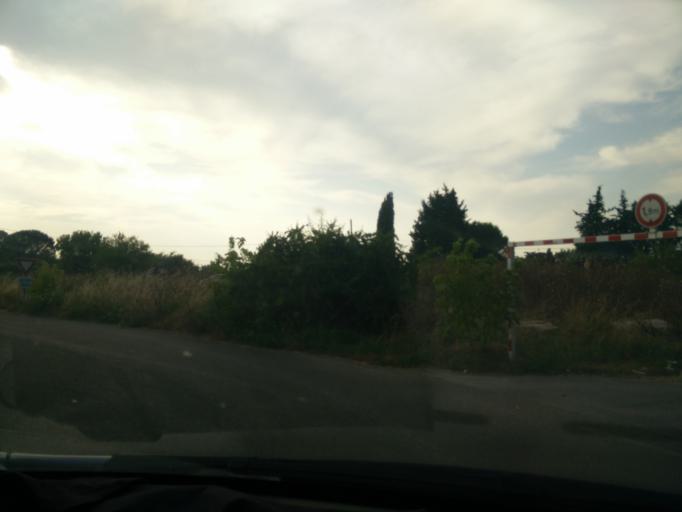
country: FR
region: Languedoc-Roussillon
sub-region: Departement du Gard
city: Gallargues-le-Montueux
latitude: 43.6918
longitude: 4.1635
